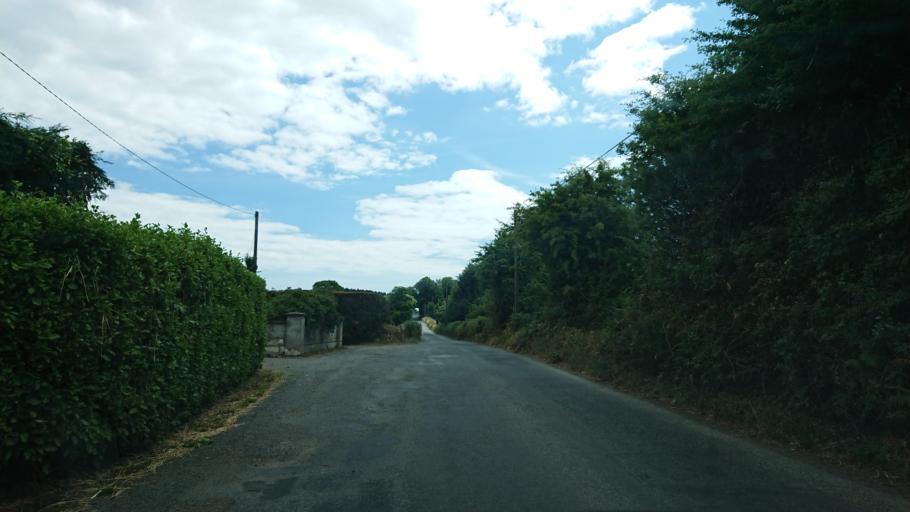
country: IE
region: Munster
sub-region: Waterford
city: Portlaw
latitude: 52.2084
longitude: -7.3310
